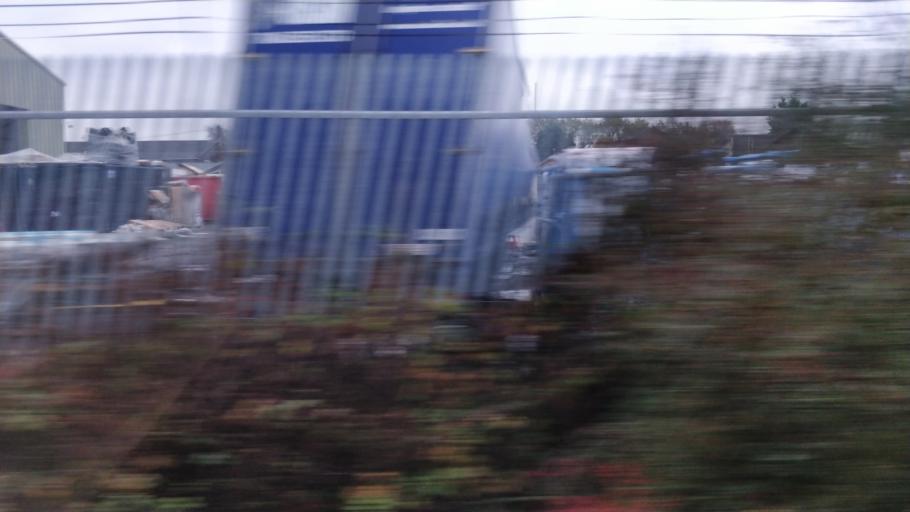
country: GB
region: England
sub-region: Borough of Wigan
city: Ince-in-Makerfield
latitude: 53.5505
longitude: -2.6511
